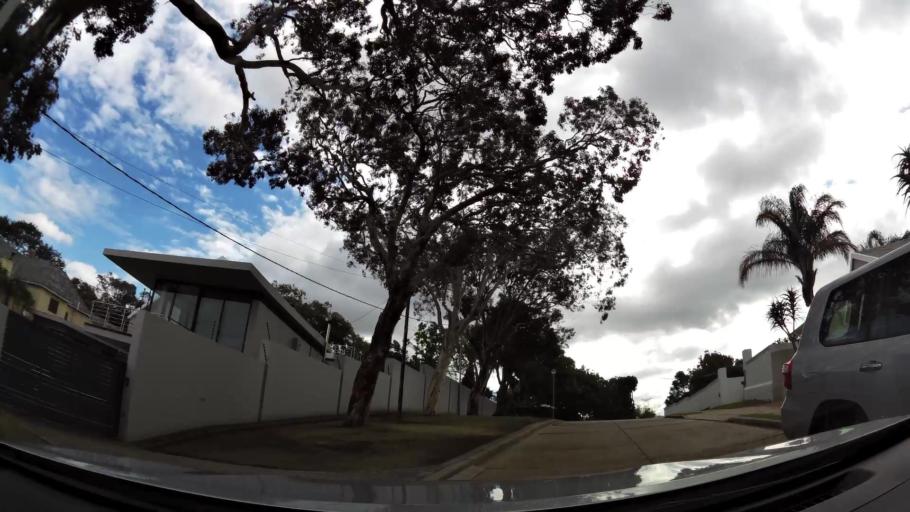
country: ZA
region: Eastern Cape
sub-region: Nelson Mandela Bay Metropolitan Municipality
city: Port Elizabeth
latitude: -33.9658
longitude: 25.5960
